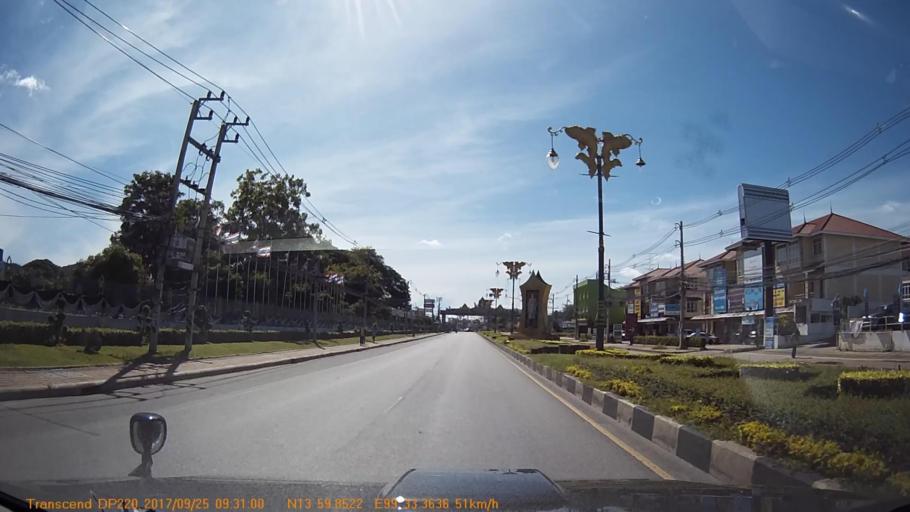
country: TH
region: Kanchanaburi
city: Kanchanaburi
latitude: 13.9974
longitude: 99.5562
